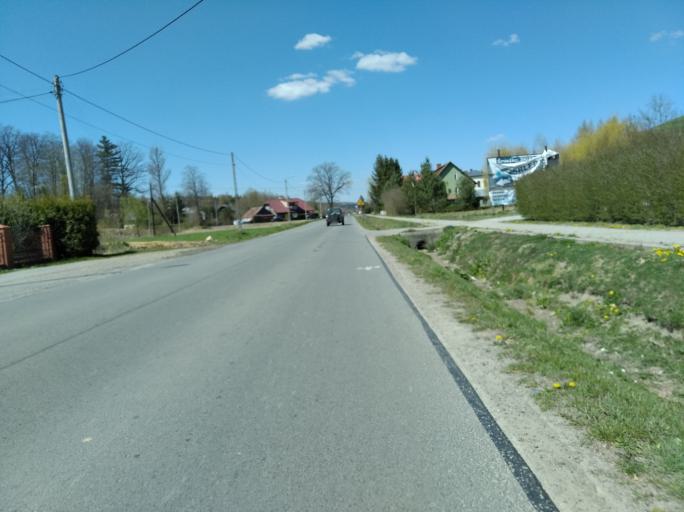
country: PL
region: Subcarpathian Voivodeship
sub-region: Powiat brzozowski
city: Dydnia
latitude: 49.6840
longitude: 22.1774
